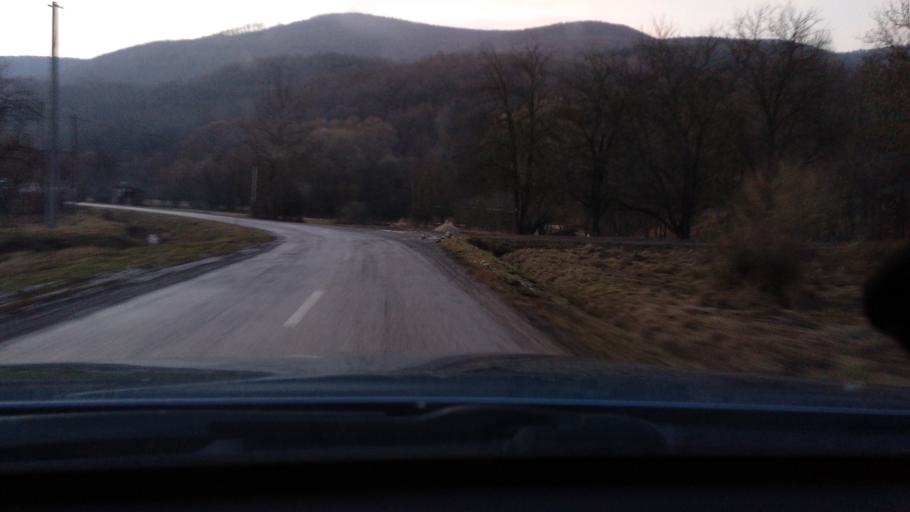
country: SK
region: Nitriansky
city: Banovce nad Bebravou
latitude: 48.8642
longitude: 18.3288
